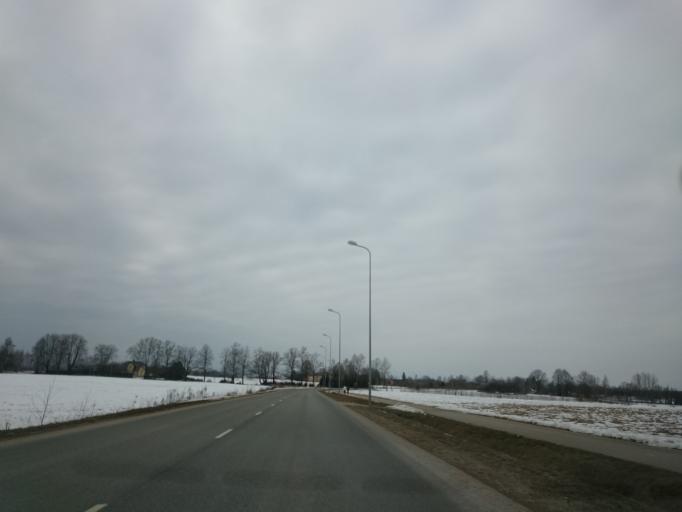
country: LV
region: Cesu Rajons
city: Cesis
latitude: 57.2967
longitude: 25.2528
